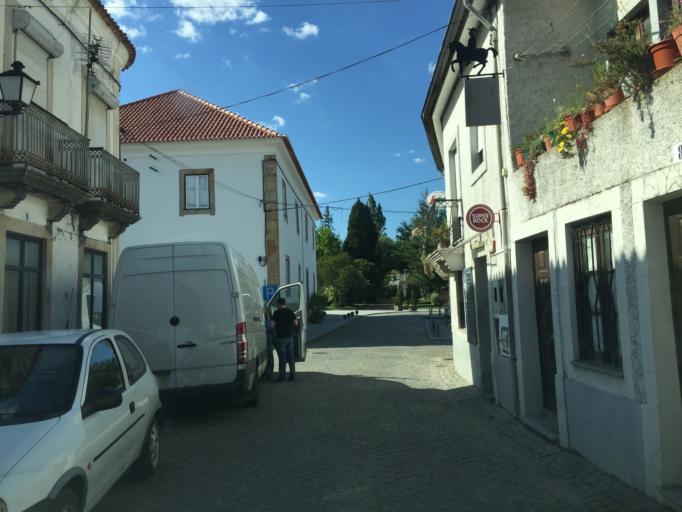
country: PT
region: Leiria
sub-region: Pedrogao Grande
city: Pedrogao Grande
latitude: 39.9177
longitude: -8.1451
